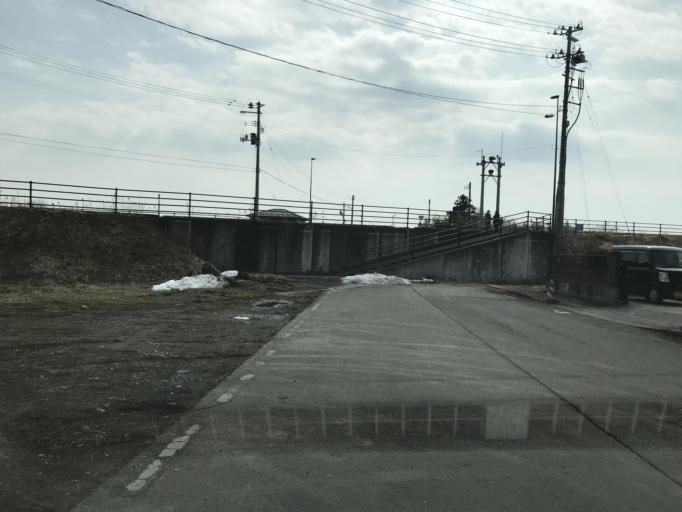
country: JP
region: Miyagi
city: Furukawa
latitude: 38.6648
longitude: 140.8668
